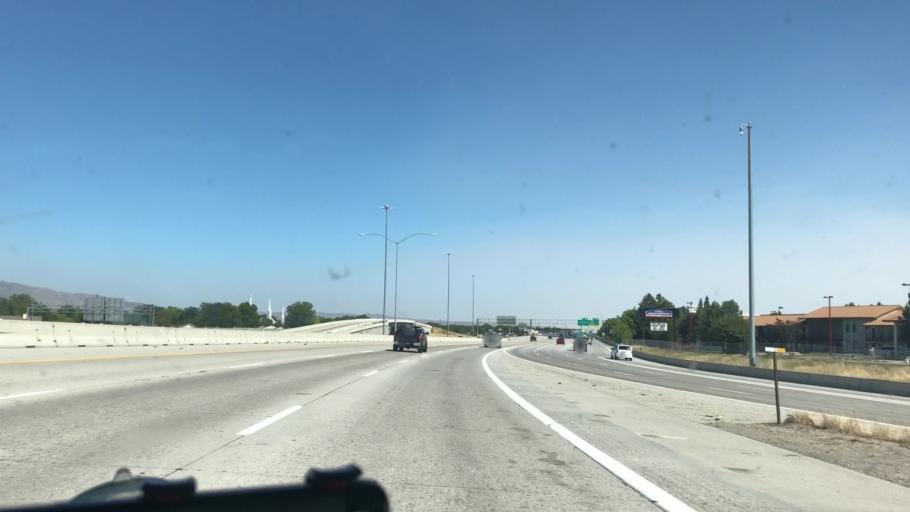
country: US
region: Idaho
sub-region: Ada County
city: Garden City
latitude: 43.5950
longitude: -116.2848
